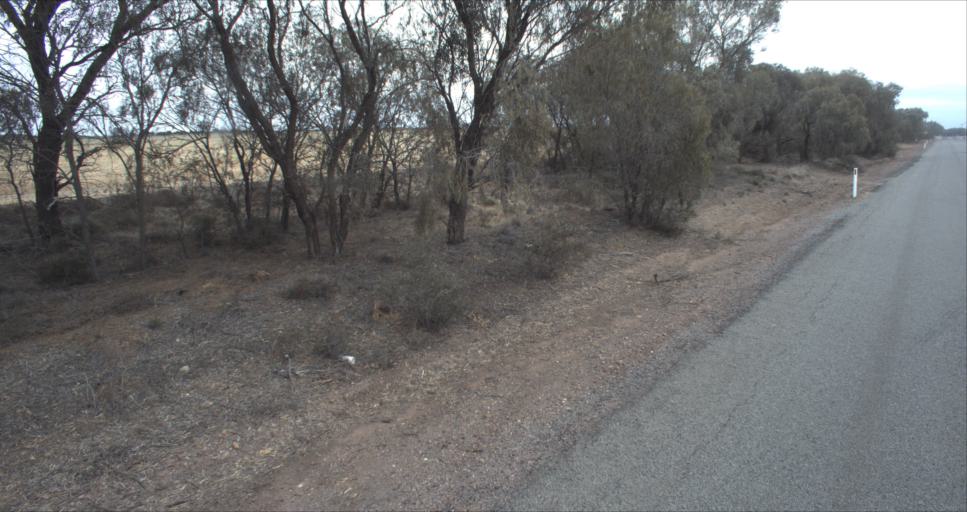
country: AU
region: New South Wales
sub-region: Leeton
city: Leeton
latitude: -34.4807
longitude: 146.3998
